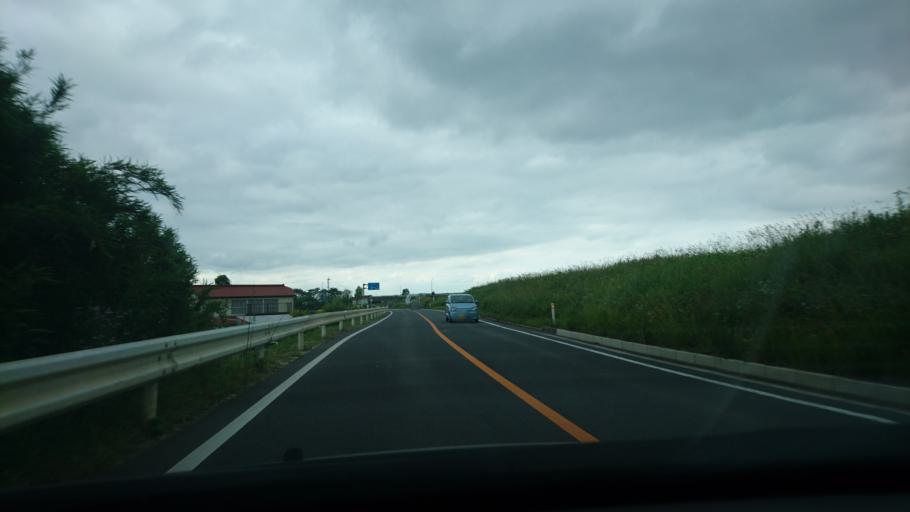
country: JP
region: Iwate
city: Ichinoseki
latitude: 38.7411
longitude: 141.1513
